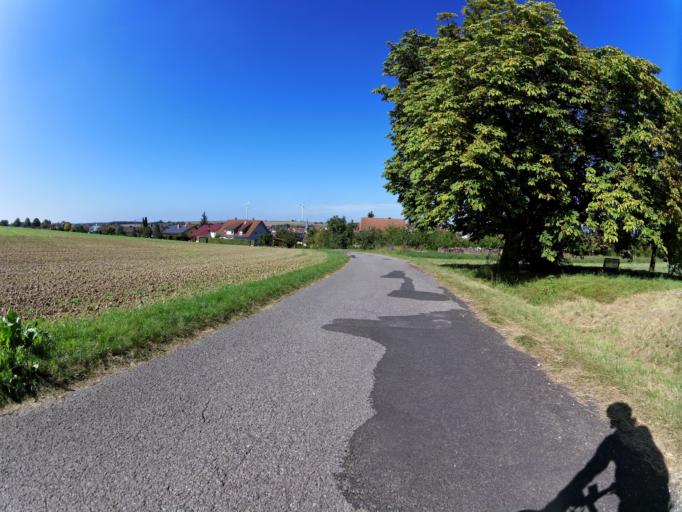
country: DE
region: Bavaria
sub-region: Regierungsbezirk Unterfranken
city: Kleinrinderfeld
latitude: 49.7041
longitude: 9.7915
